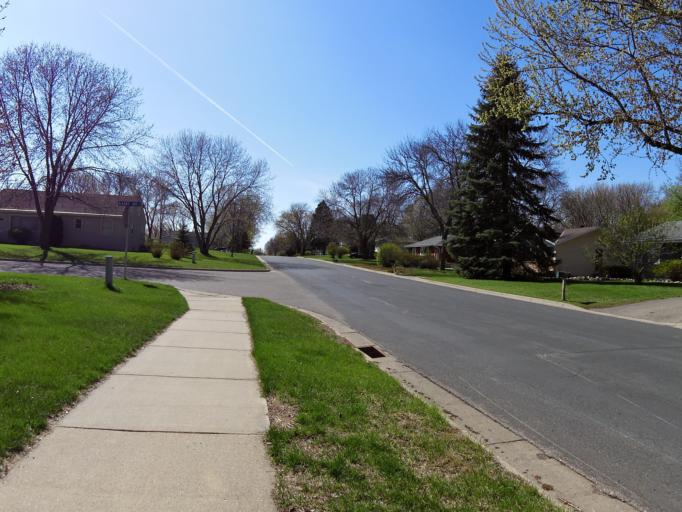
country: US
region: Minnesota
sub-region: Scott County
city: Prior Lake
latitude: 44.7127
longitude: -93.4332
